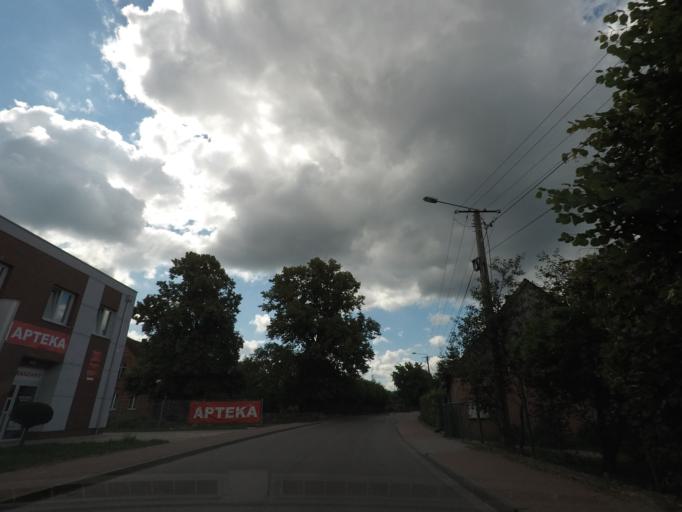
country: PL
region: Pomeranian Voivodeship
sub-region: Powiat wejherowski
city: Leczyce
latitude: 54.5902
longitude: 17.8621
